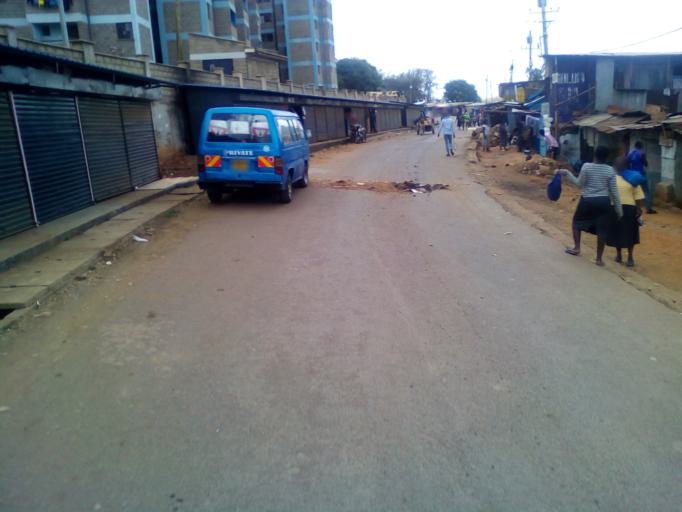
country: KE
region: Nairobi Area
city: Nairobi
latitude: -1.3150
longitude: 36.8010
